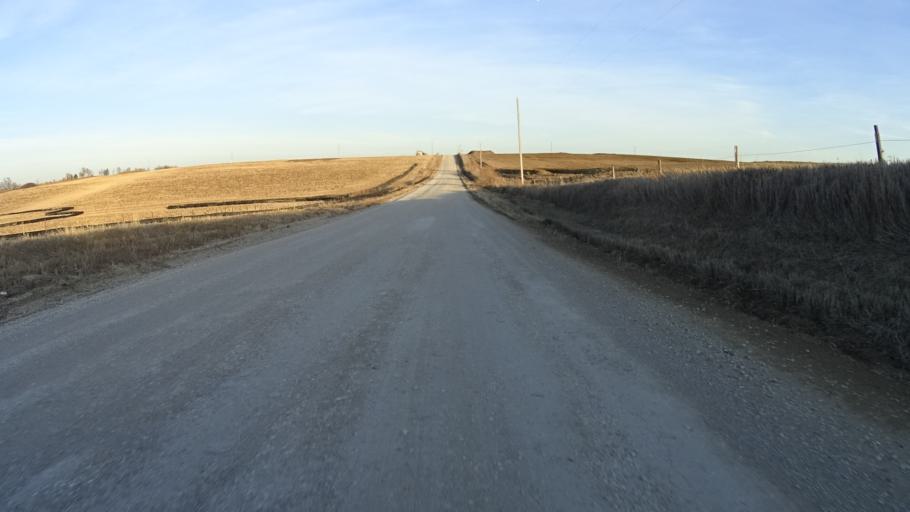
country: US
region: Nebraska
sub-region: Sarpy County
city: Springfield
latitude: 41.1326
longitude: -96.1003
